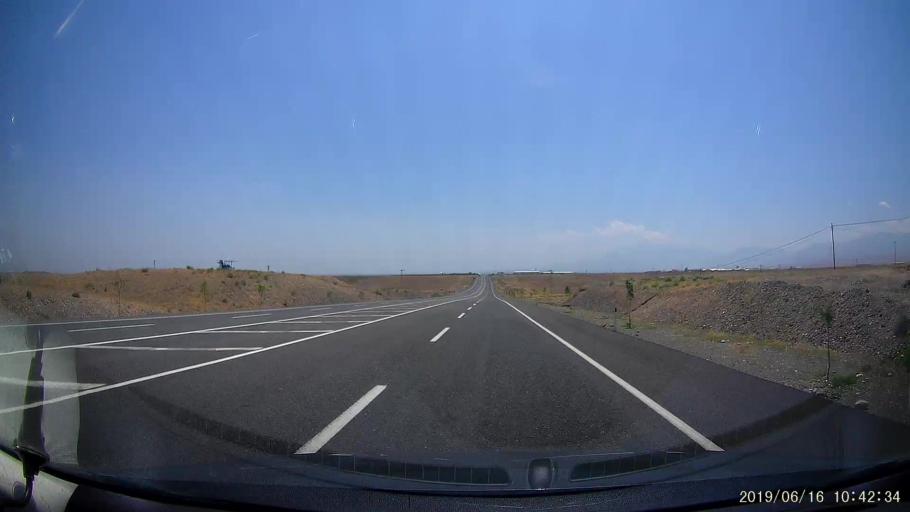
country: AM
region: Armavir
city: Shenavan
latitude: 40.0410
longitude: 43.8101
